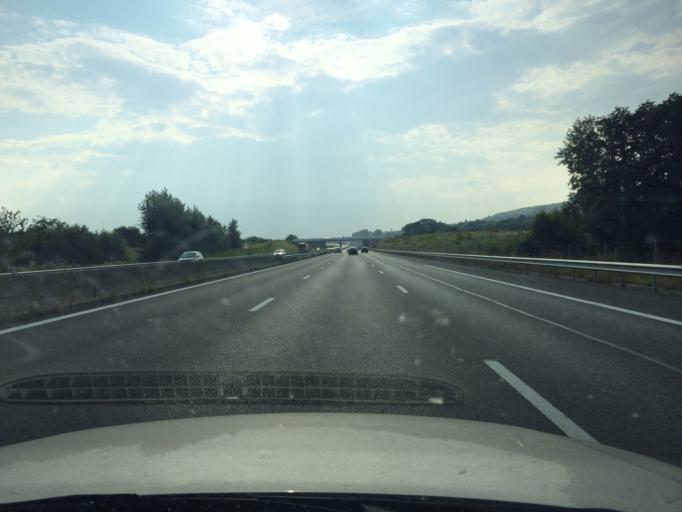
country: FR
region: Lower Normandy
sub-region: Departement du Calvados
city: Saint-Gatien-des-Bois
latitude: 49.2997
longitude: 0.2502
